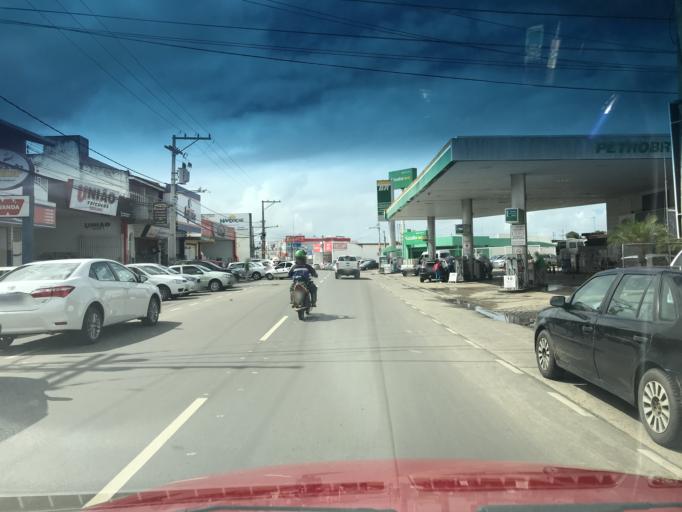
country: BR
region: Bahia
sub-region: Santo Antonio De Jesus
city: Santo Antonio de Jesus
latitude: -12.9661
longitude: -39.2711
